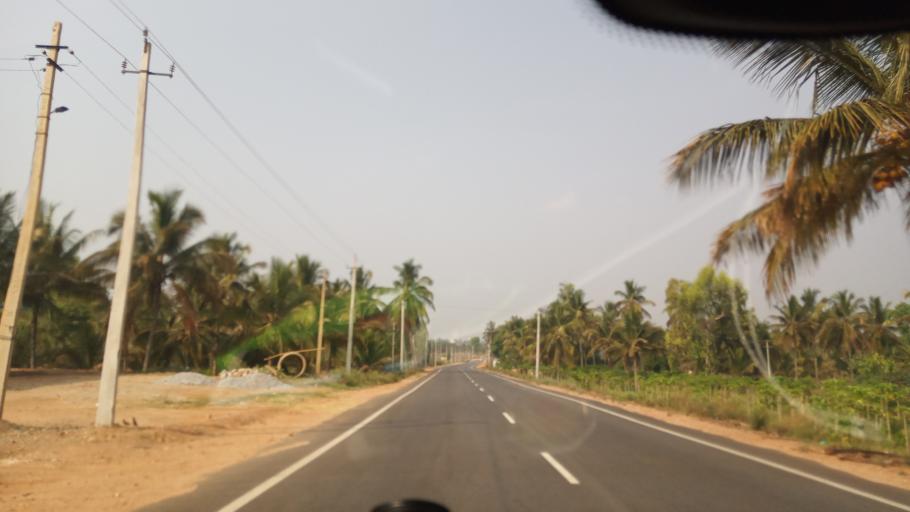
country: IN
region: Karnataka
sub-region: Mandya
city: Melukote
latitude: 12.7169
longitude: 76.7085
